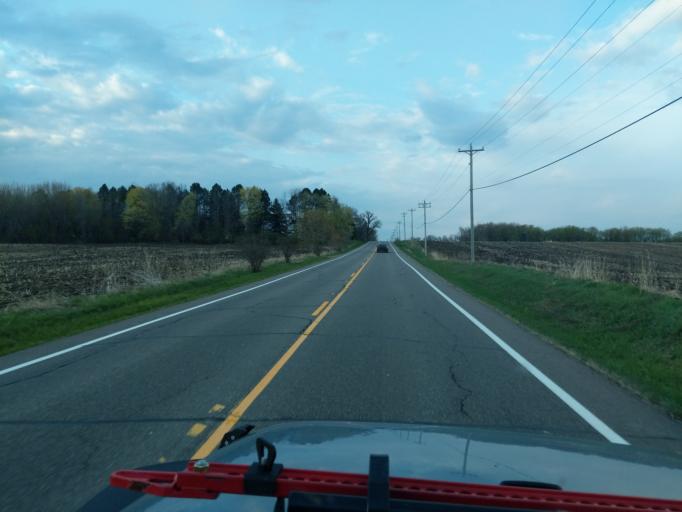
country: US
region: Minnesota
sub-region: Hennepin County
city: Rogers
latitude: 45.1508
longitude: -93.5219
